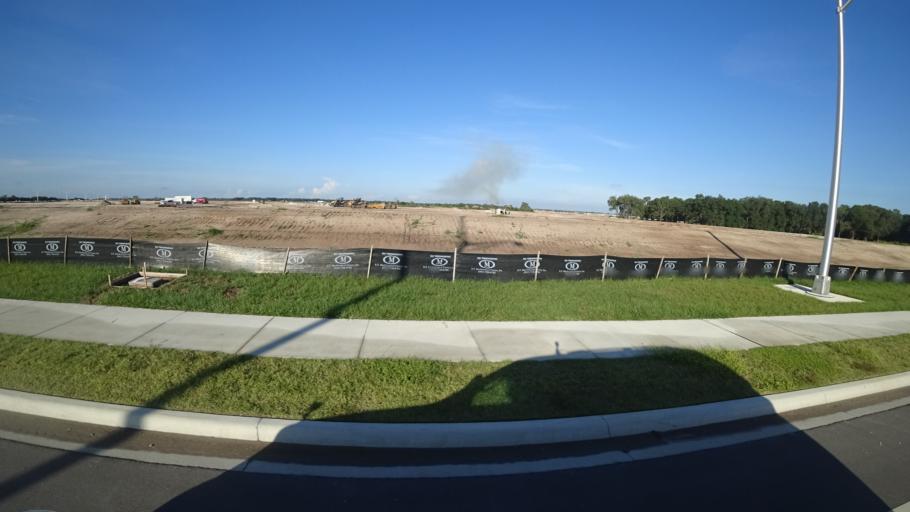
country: US
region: Florida
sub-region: Sarasota County
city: The Meadows
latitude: 27.4499
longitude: -82.3718
